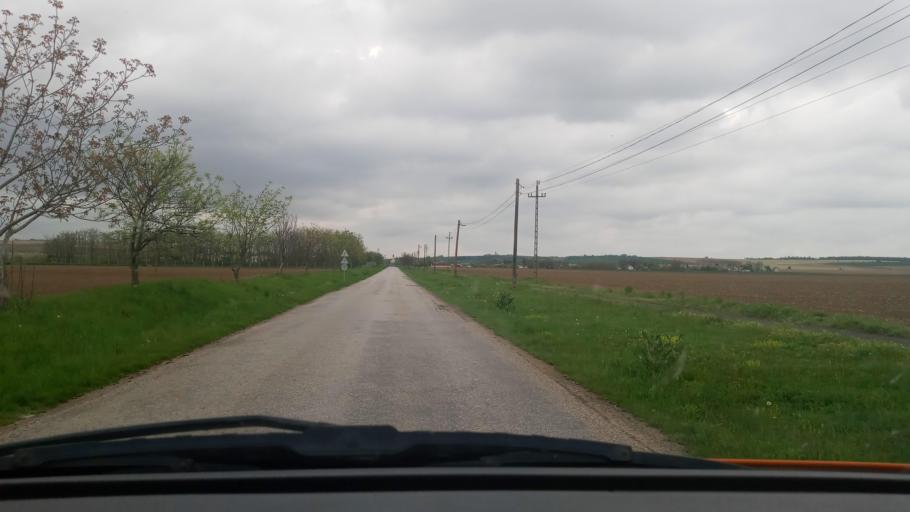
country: HU
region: Baranya
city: Boly
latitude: 45.9897
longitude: 18.5603
